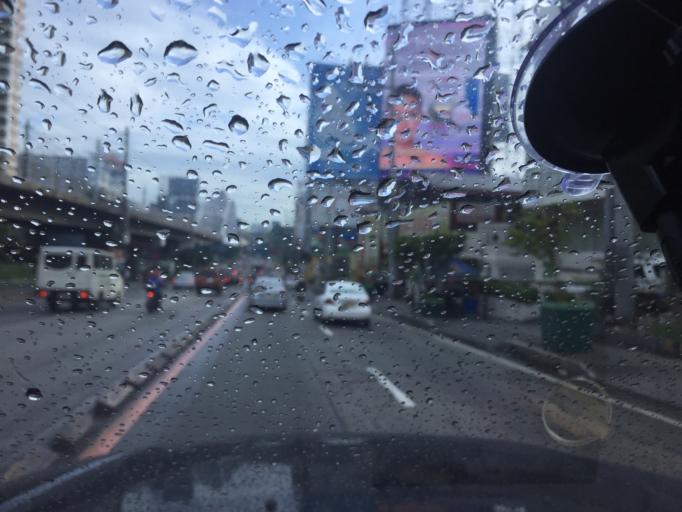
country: PH
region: Metro Manila
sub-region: Mandaluyong
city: Mandaluyong City
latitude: 14.5700
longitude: 121.0463
